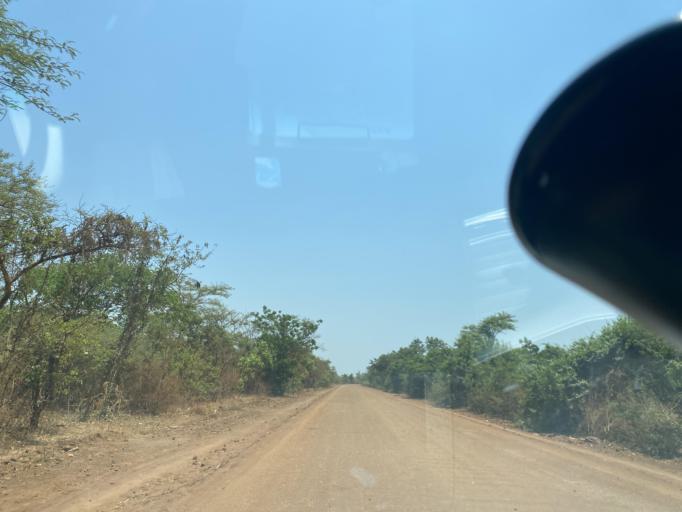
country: ZM
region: Southern
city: Nakambala
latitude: -15.4931
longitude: 27.9053
